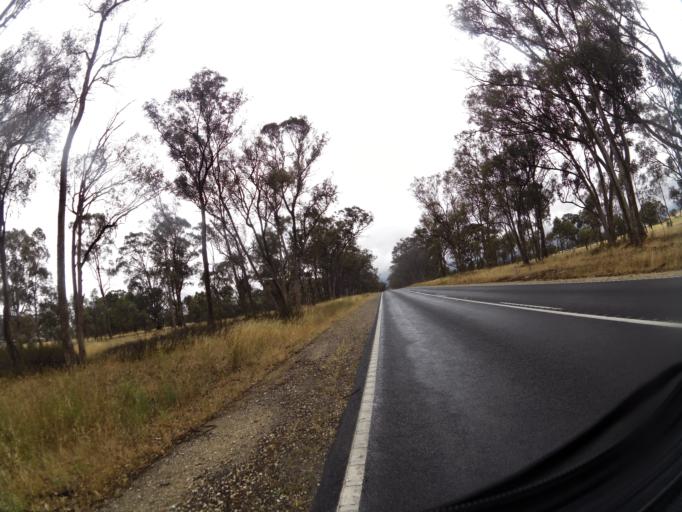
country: AU
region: Victoria
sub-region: Mount Alexander
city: Castlemaine
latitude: -37.0906
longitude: 144.1445
